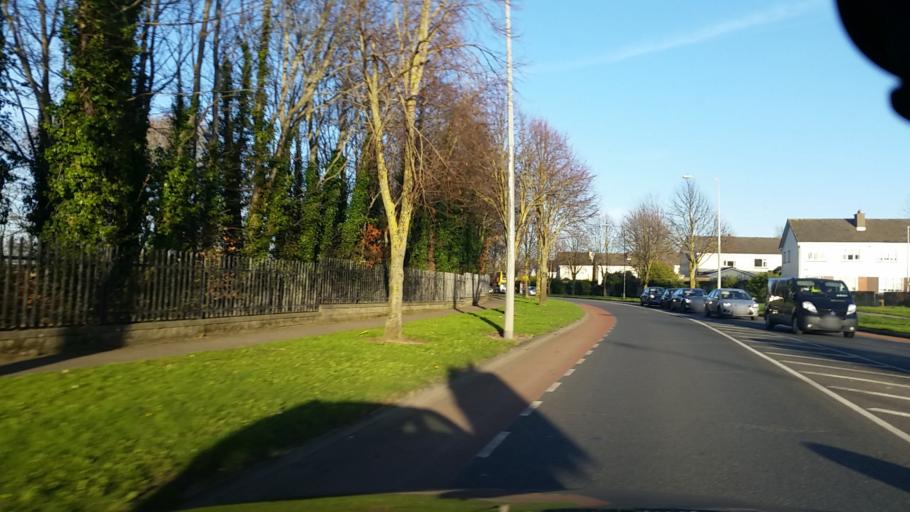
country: IE
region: Leinster
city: Hartstown
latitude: 53.3909
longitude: -6.4129
